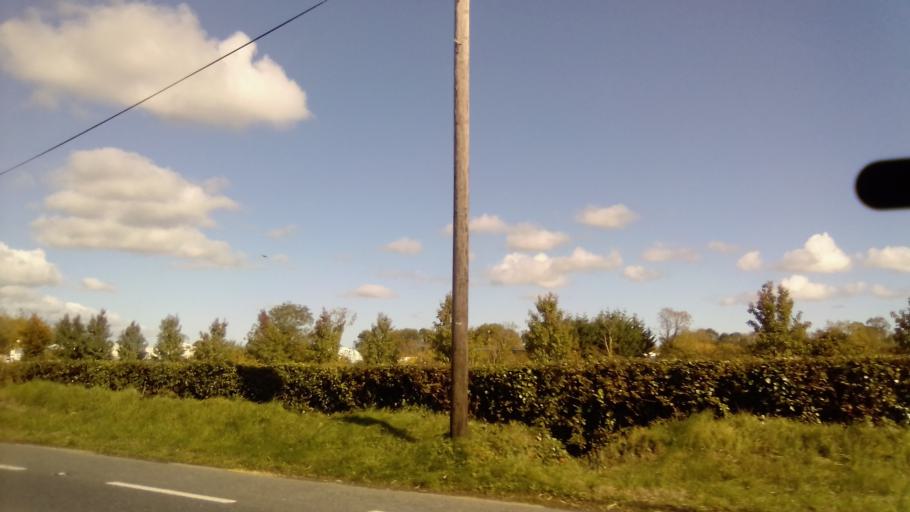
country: IE
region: Leinster
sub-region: An Mhi
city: Ratoath
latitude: 53.5499
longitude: -6.4340
